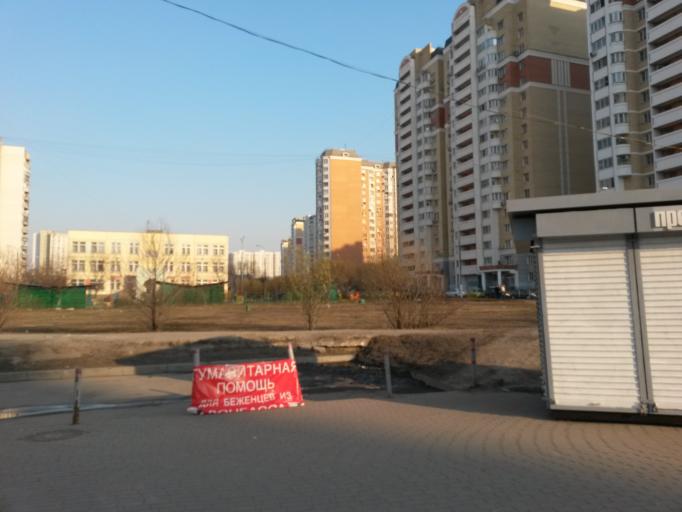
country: RU
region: Moscow
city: Annino
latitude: 55.5679
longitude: 37.5764
